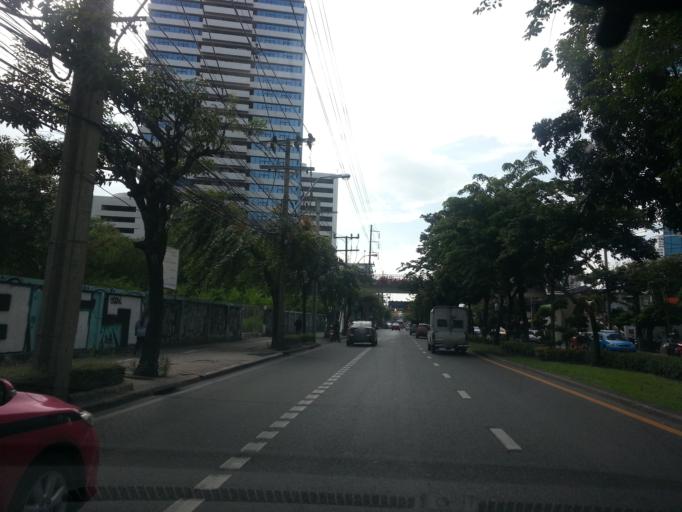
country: TH
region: Bangkok
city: Khlong Toei
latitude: 13.7168
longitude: 100.5721
